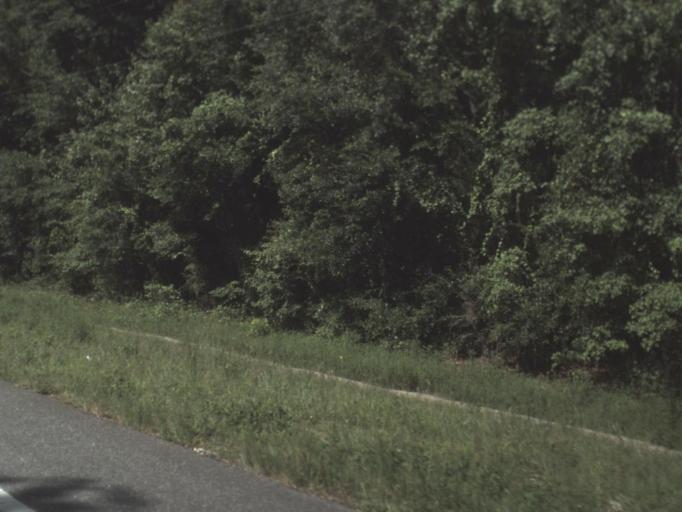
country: US
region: Florida
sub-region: Alachua County
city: High Springs
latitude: 29.8390
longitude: -82.7417
